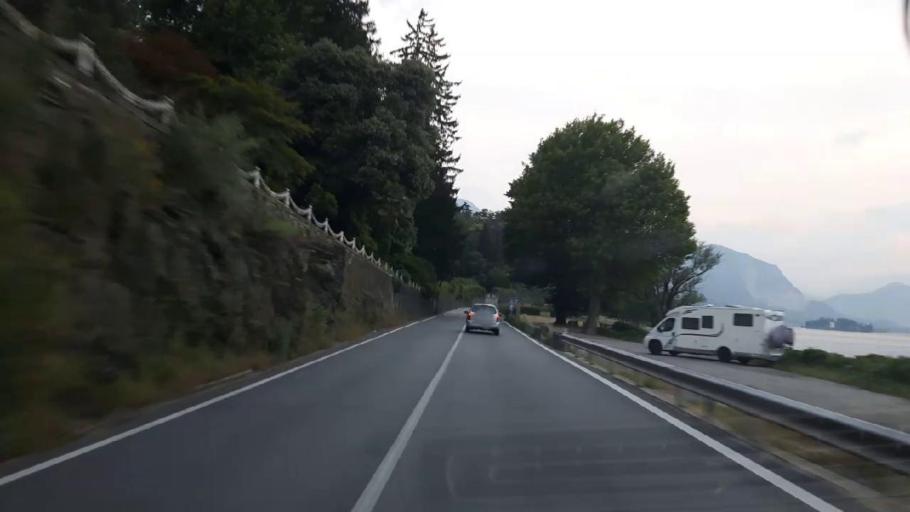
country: IT
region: Piedmont
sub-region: Provincia Verbano-Cusio-Ossola
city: Stresa
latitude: 45.8808
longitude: 8.5521
